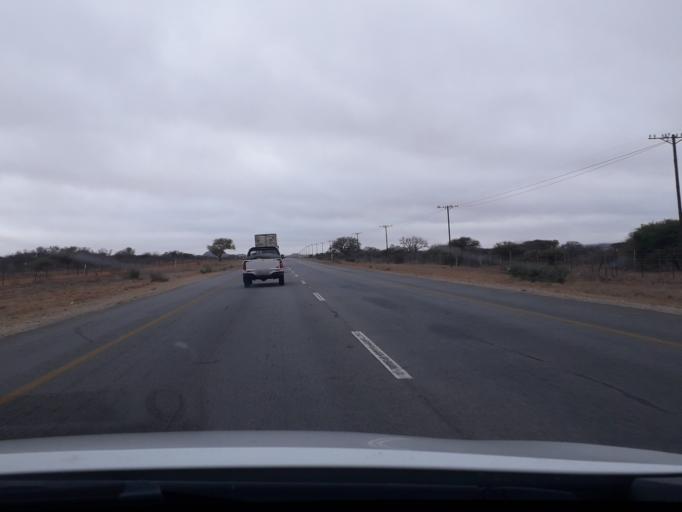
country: ZA
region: Limpopo
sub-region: Capricorn District Municipality
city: Mankoeng
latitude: -23.5686
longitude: 29.6776
